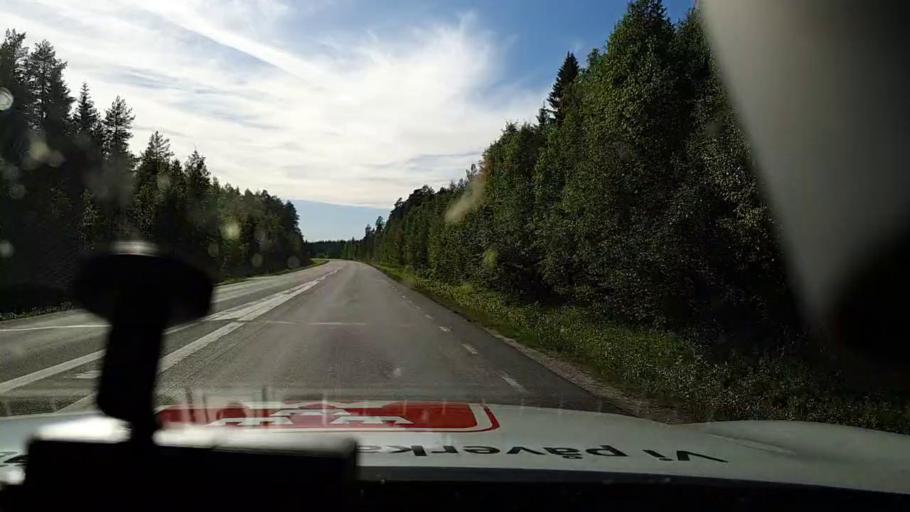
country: SE
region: Norrbotten
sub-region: Lulea Kommun
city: Gammelstad
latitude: 65.6627
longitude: 22.0894
